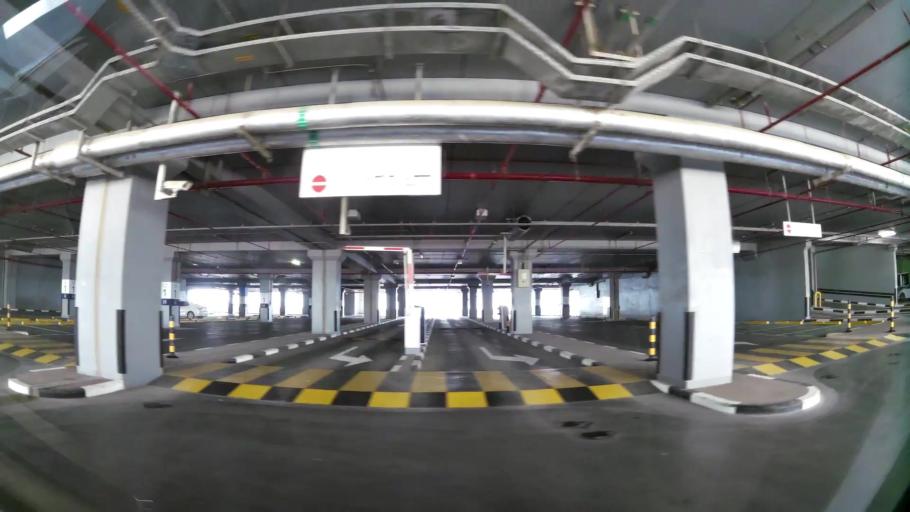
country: AE
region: Ash Shariqah
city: Sharjah
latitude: 25.2543
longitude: 55.4025
